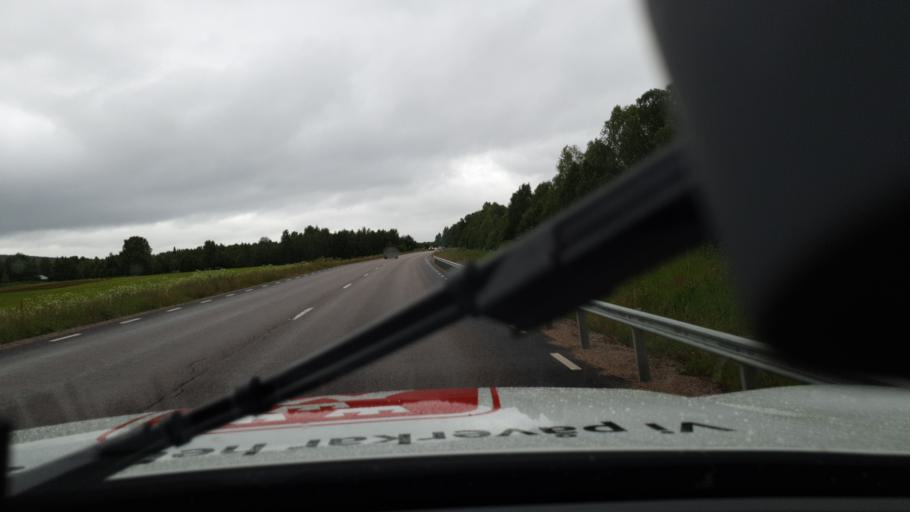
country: SE
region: Norrbotten
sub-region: Overtornea Kommun
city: OEvertornea
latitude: 66.4163
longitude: 23.6255
